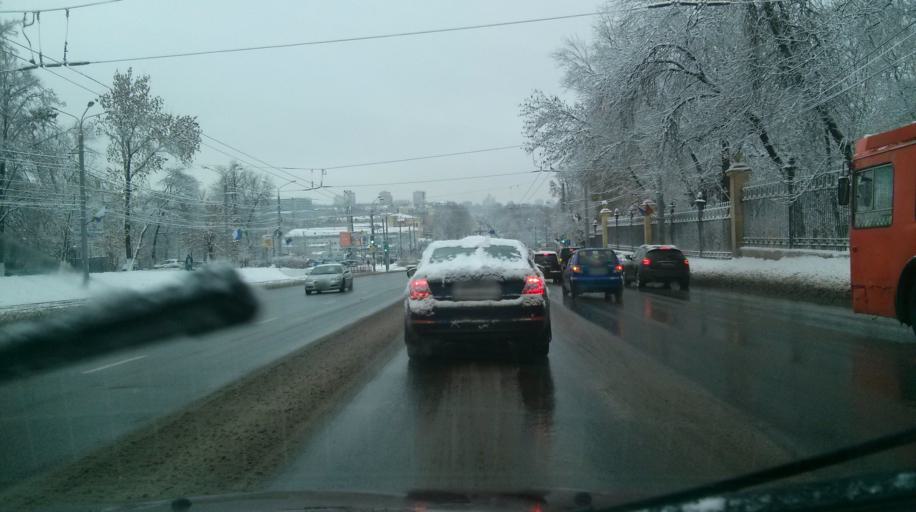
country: RU
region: Nizjnij Novgorod
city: Nizhniy Novgorod
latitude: 56.2580
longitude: 43.9717
